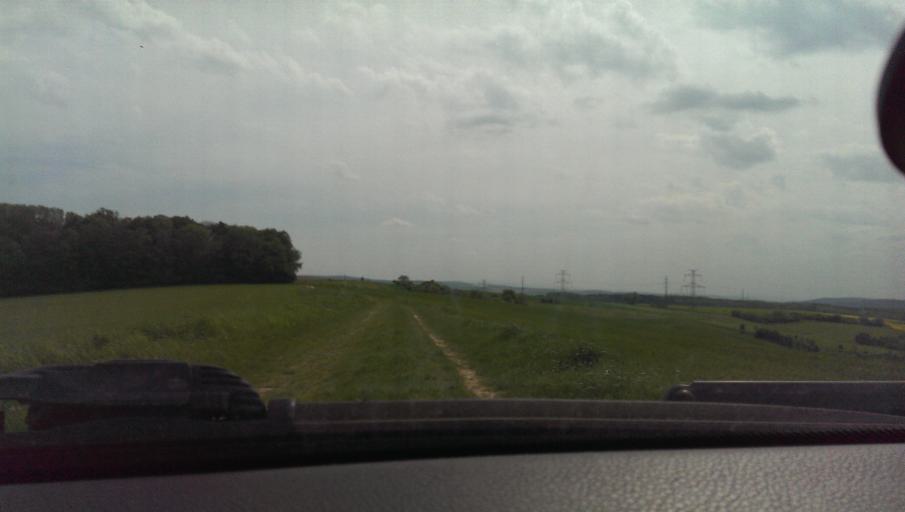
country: CZ
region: Zlin
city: Tlumacov
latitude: 49.2618
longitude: 17.5319
